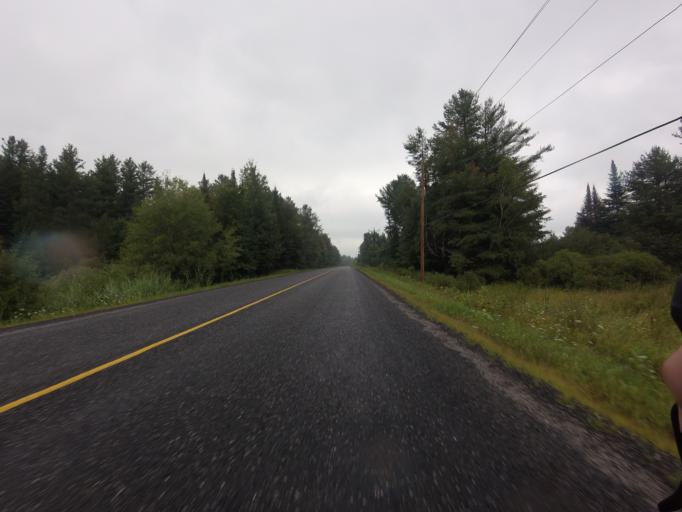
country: CA
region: Ontario
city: Perth
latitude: 45.0627
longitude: -76.5138
